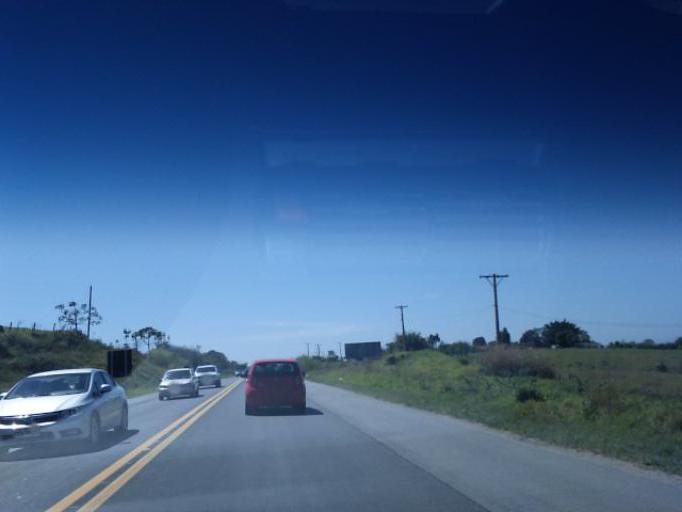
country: BR
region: Sao Paulo
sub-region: Tremembe
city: Tremembe
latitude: -22.9550
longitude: -45.6231
